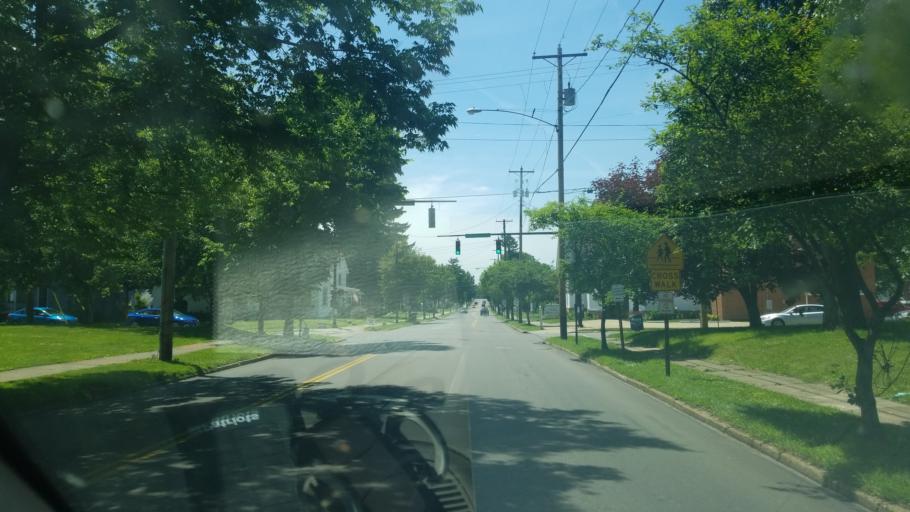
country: US
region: Ohio
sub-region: Stark County
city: Louisville
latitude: 40.8386
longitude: -81.2498
